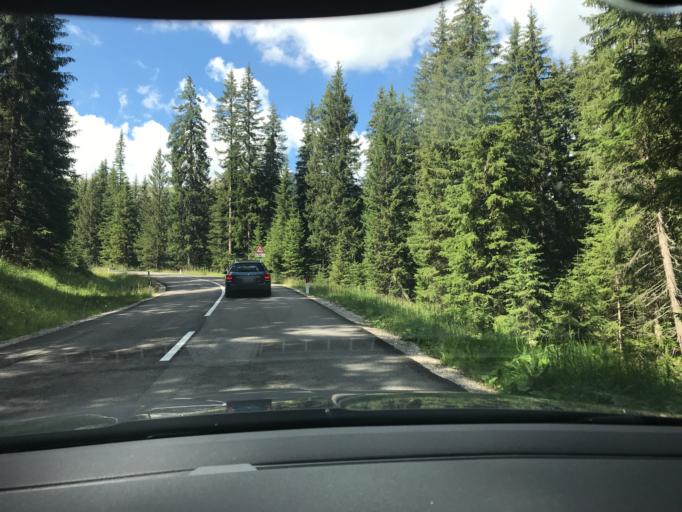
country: IT
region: Veneto
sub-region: Provincia di Belluno
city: Livinallongo del Col di Lana
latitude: 46.5513
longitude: 11.9681
